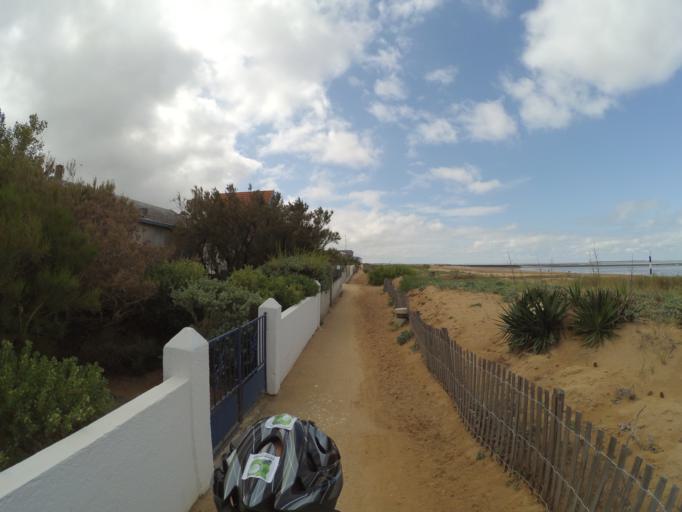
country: FR
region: Poitou-Charentes
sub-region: Departement de la Charente-Maritime
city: Chatelaillon-Plage
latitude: 46.0674
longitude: -1.0929
